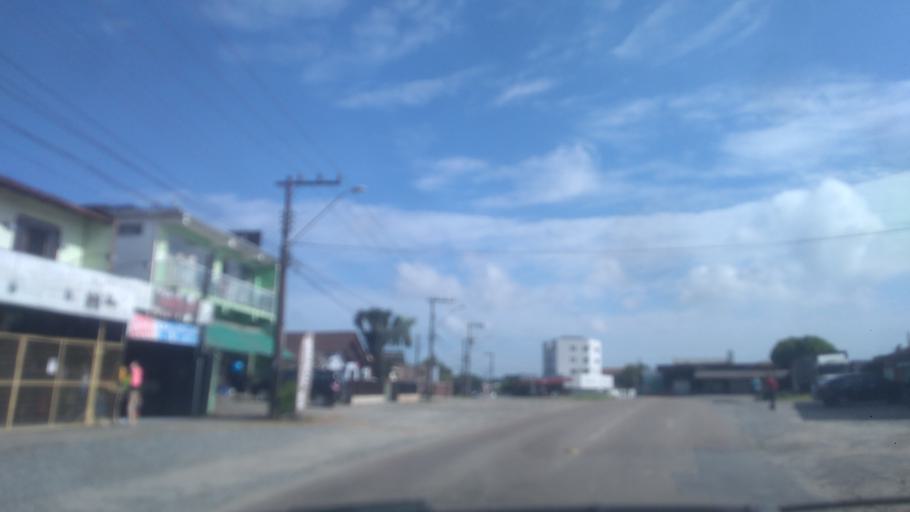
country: BR
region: Santa Catarina
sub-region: Joinville
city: Joinville
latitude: -26.3249
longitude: -48.8083
